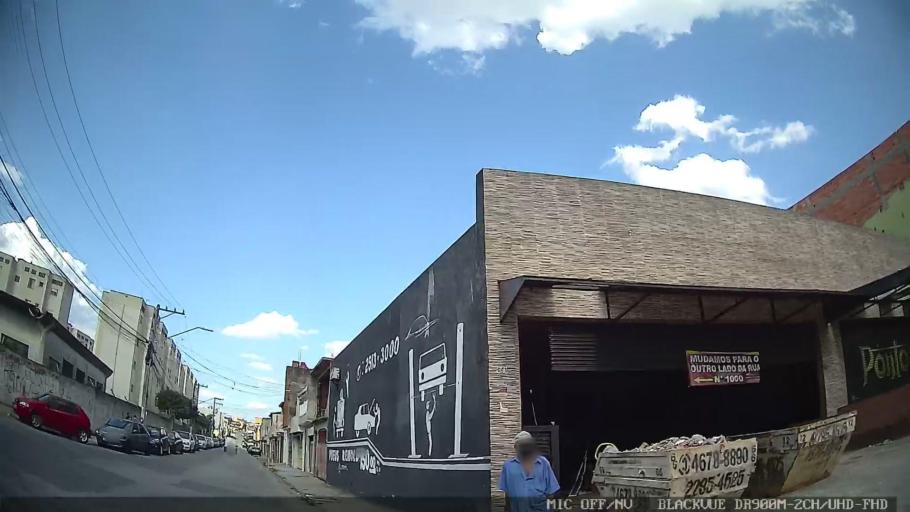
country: BR
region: Sao Paulo
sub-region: Ferraz De Vasconcelos
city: Ferraz de Vasconcelos
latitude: -23.5236
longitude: -46.4303
